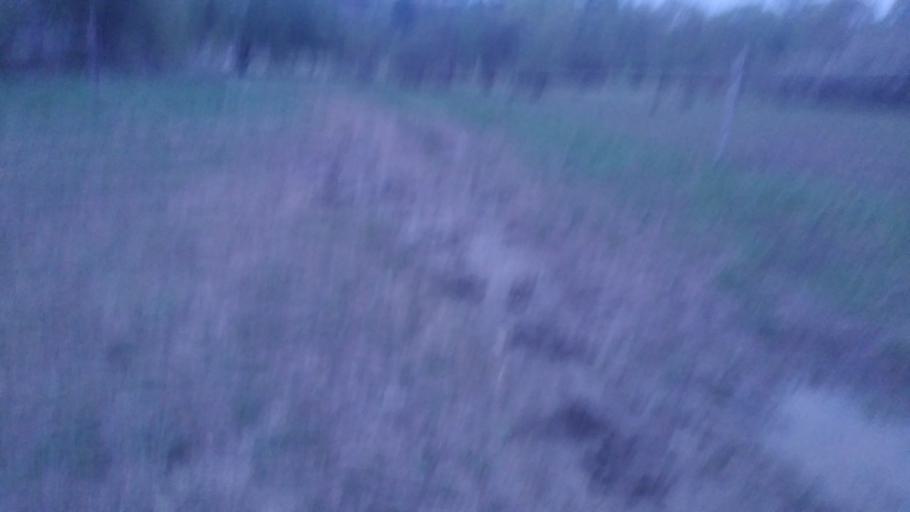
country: HU
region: Pest
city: Pomaz
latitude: 47.6295
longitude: 19.0232
